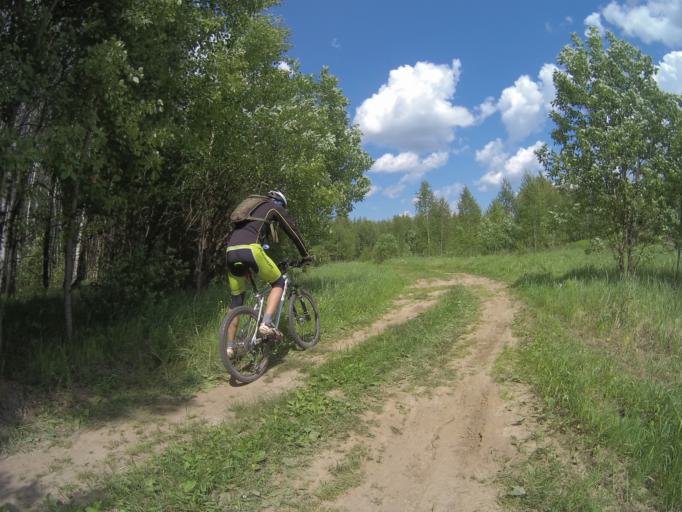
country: RU
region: Vladimir
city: Raduzhnyy
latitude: 56.0167
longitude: 40.2318
